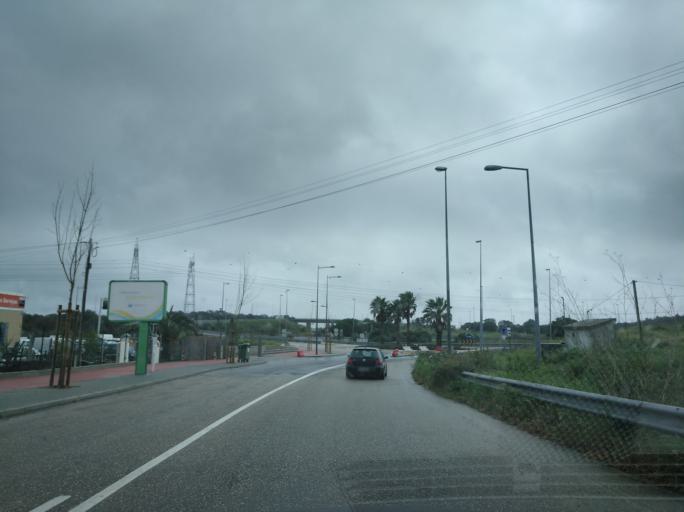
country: PT
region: Setubal
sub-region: Grandola
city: Grandola
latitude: 38.1699
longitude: -8.5557
